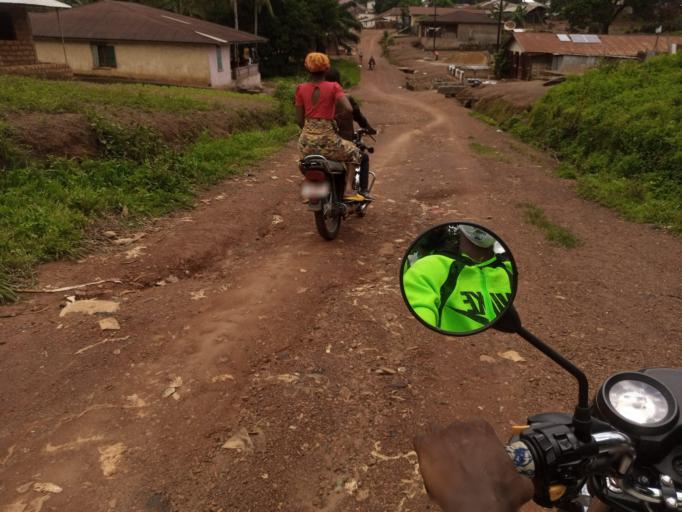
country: SL
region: Northern Province
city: Port Loko
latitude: 8.7626
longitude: -12.7830
